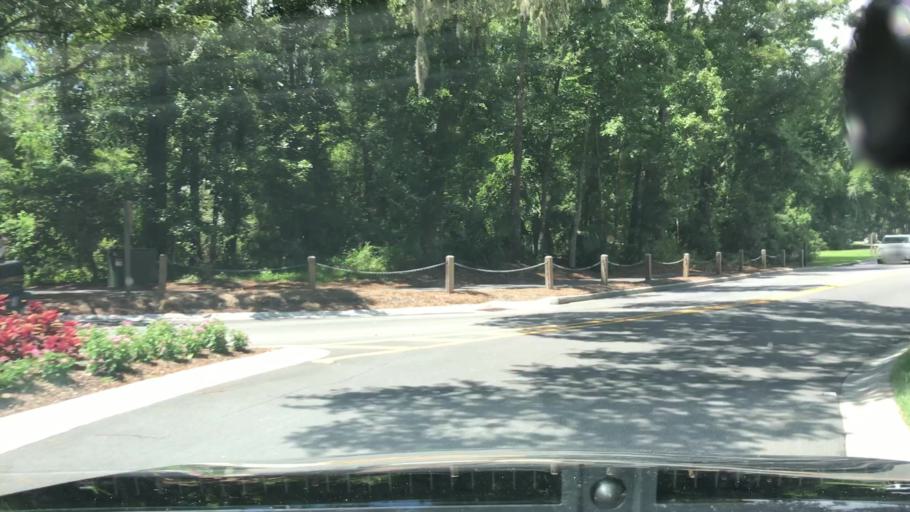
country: US
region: South Carolina
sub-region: Beaufort County
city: Hilton Head Island
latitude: 32.1318
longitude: -80.7966
